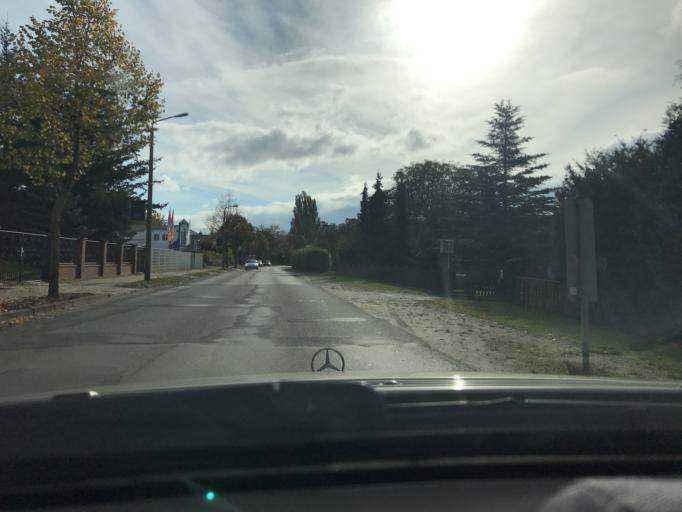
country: DE
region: Mecklenburg-Vorpommern
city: Ostseebad Zinnowitz
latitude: 54.0726
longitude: 13.9094
